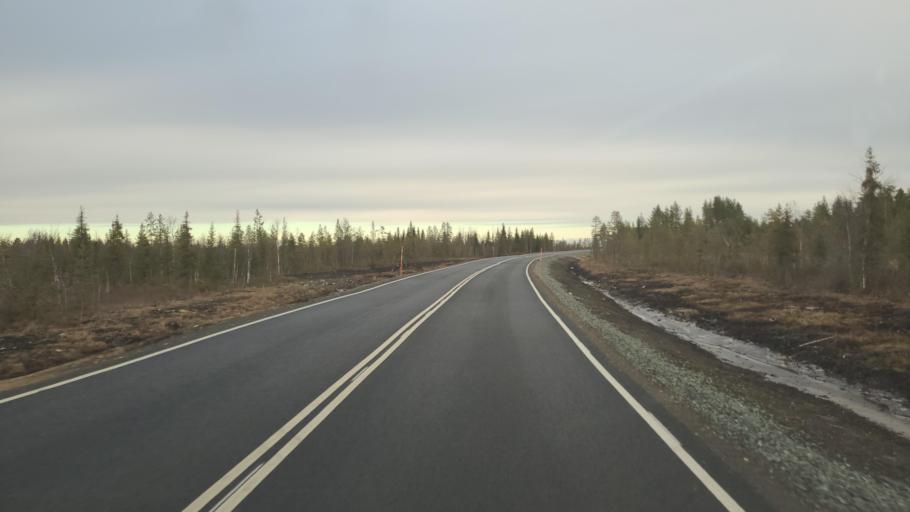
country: FI
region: Lapland
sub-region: Tunturi-Lappi
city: Kittilae
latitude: 67.8812
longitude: 25.0386
